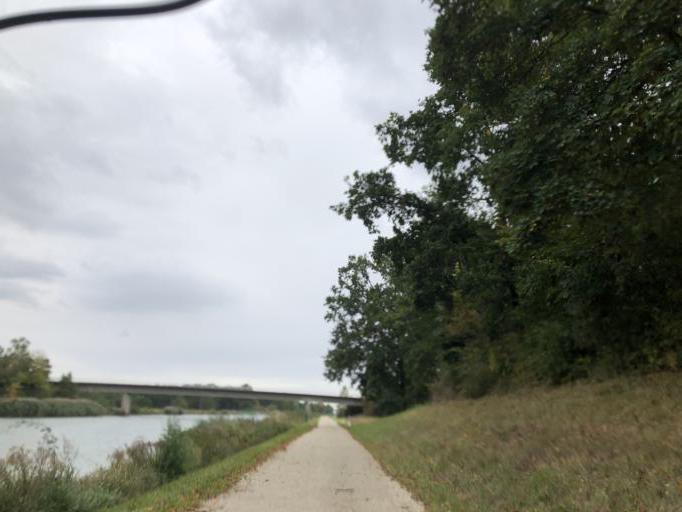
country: DE
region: Bavaria
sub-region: Regierungsbezirk Mittelfranken
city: Obermichelbach
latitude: 49.5437
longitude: 10.9686
